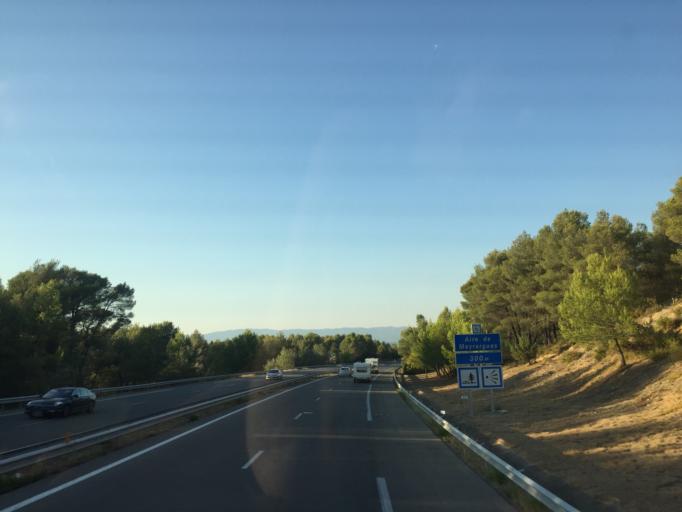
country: FR
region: Provence-Alpes-Cote d'Azur
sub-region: Departement des Bouches-du-Rhone
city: Venelles
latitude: 43.6255
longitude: 5.4924
